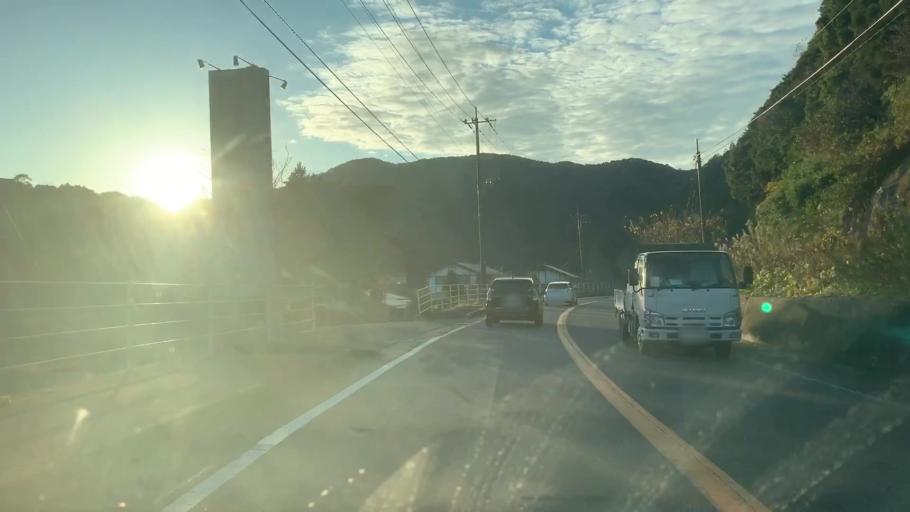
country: JP
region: Saga Prefecture
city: Karatsu
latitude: 33.3369
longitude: 129.9772
